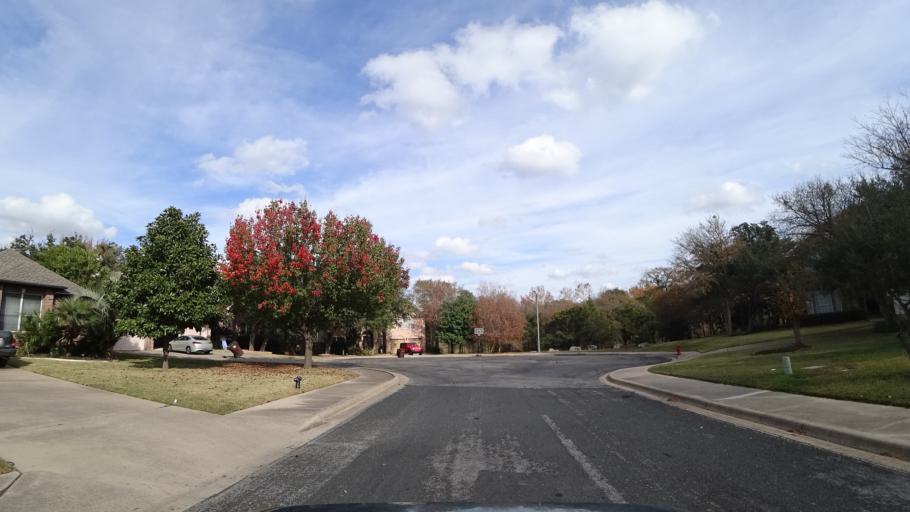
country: US
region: Texas
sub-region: Williamson County
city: Brushy Creek
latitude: 30.5161
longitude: -97.7434
